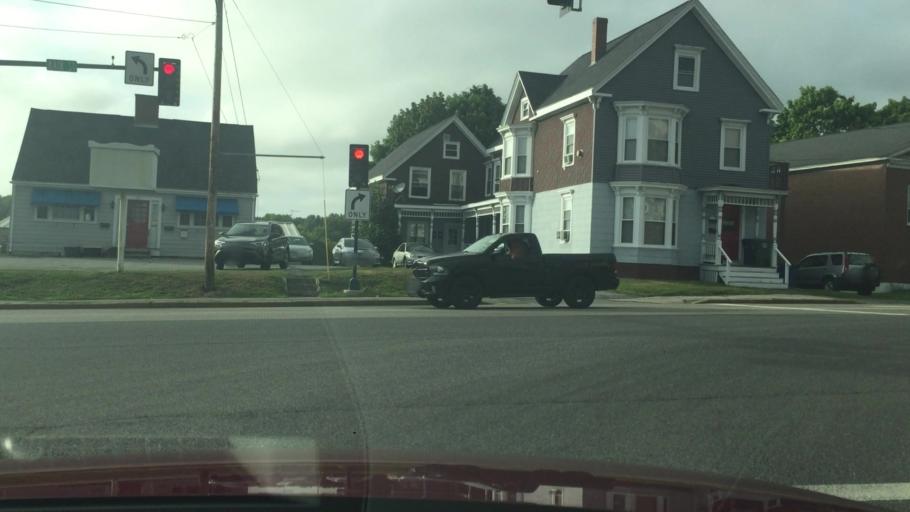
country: US
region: Maine
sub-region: Cumberland County
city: Westbrook
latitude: 43.6792
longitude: -70.3545
